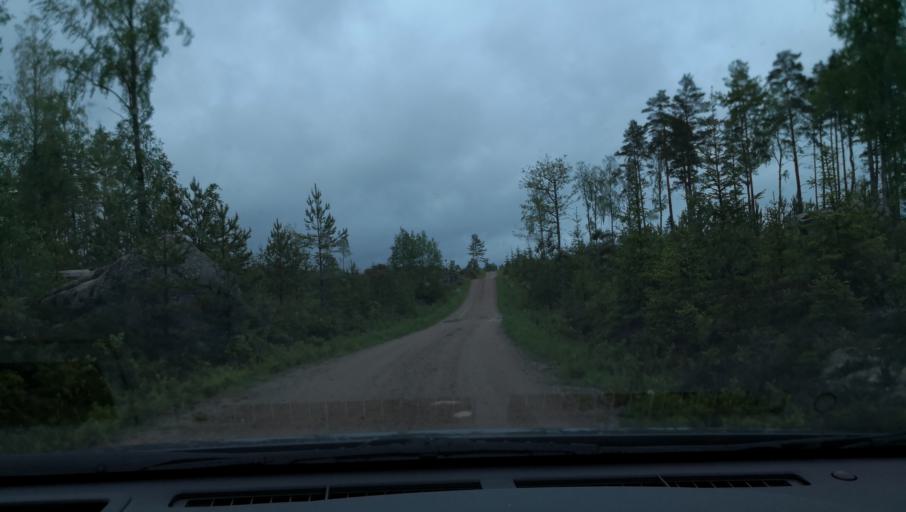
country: SE
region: Uppsala
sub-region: Enkopings Kommun
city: Orsundsbro
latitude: 59.9369
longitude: 17.3124
